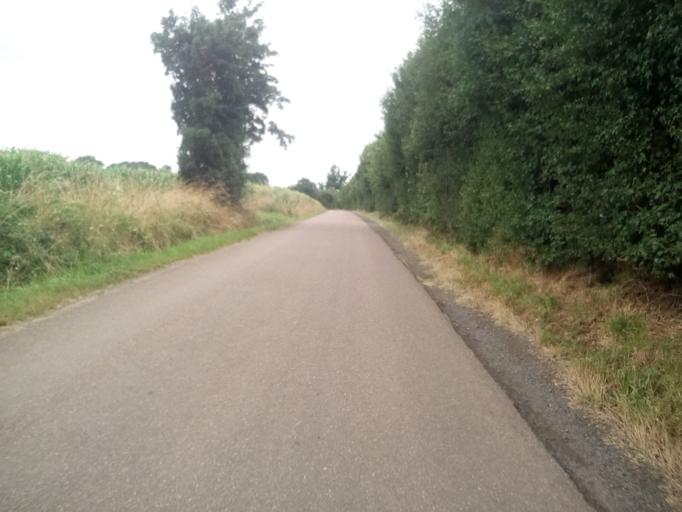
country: FR
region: Lower Normandy
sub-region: Departement du Calvados
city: Clinchamps-sur-Orne
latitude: 49.0384
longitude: -0.3935
